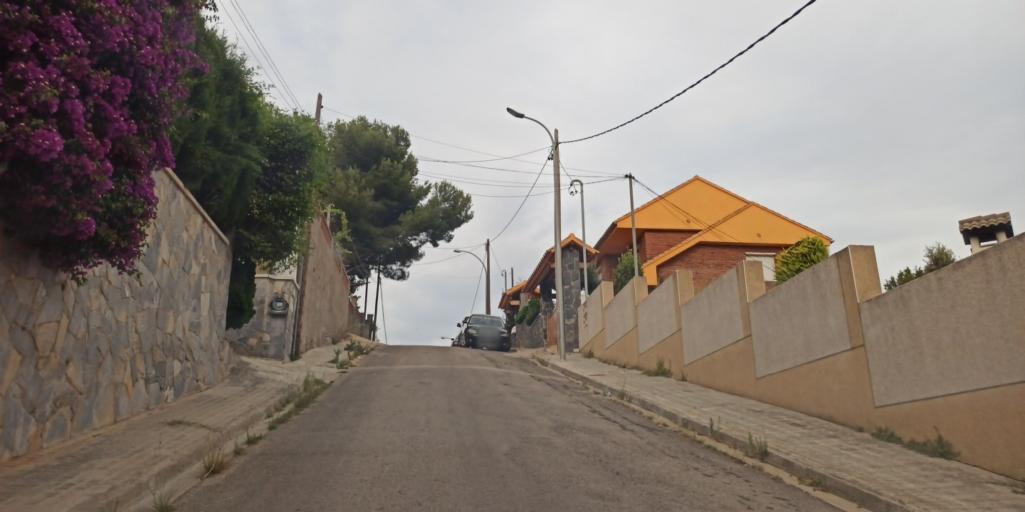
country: ES
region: Catalonia
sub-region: Provincia de Barcelona
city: Castelldefels
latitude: 41.2847
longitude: 1.9659
